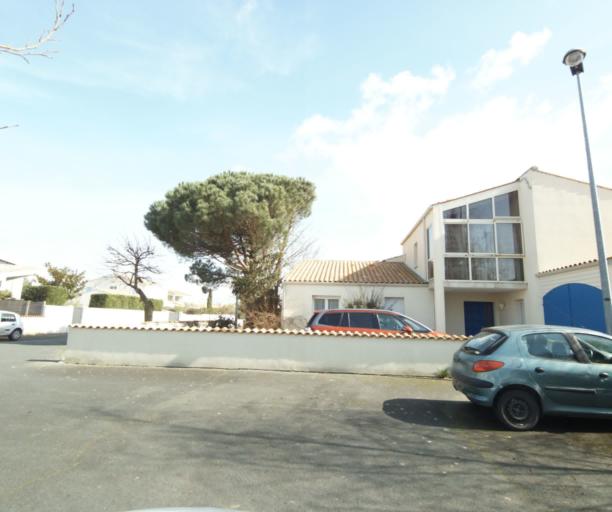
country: FR
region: Poitou-Charentes
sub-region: Departement de la Charente-Maritime
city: Lagord
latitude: 46.1837
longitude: -1.1659
